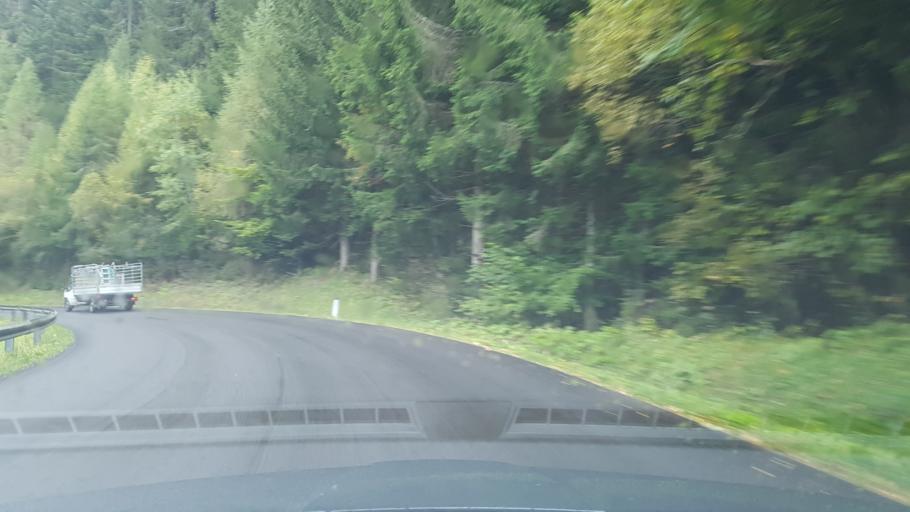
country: AT
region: Styria
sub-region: Politischer Bezirk Voitsberg
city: Salla
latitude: 47.1098
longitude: 14.9445
